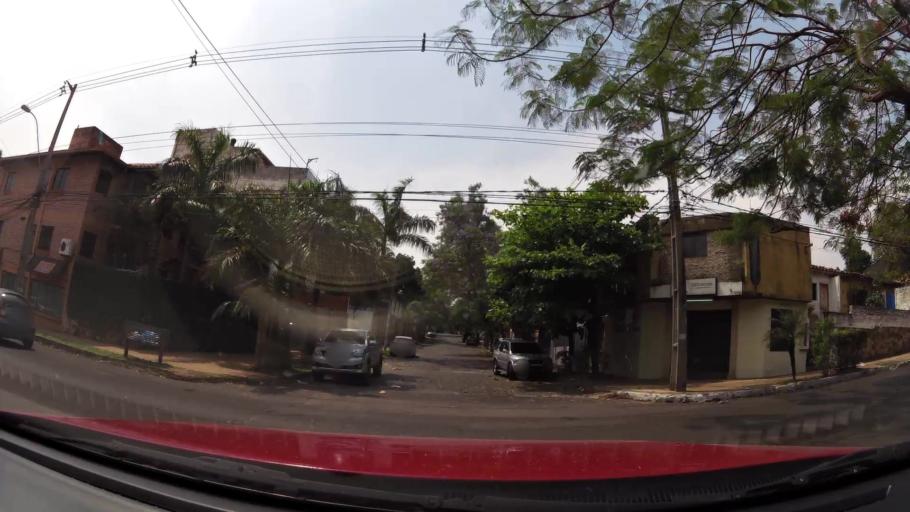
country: PY
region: Asuncion
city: Asuncion
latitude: -25.2782
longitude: -57.5983
